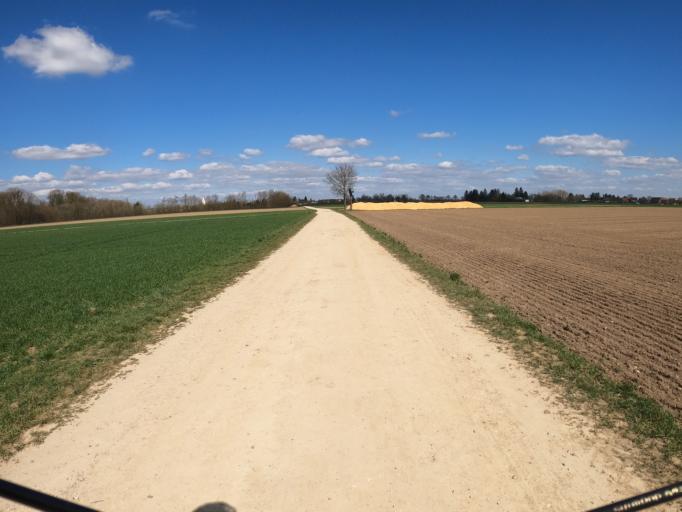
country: DE
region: Bavaria
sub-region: Swabia
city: Nersingen
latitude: 48.4226
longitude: 10.1517
